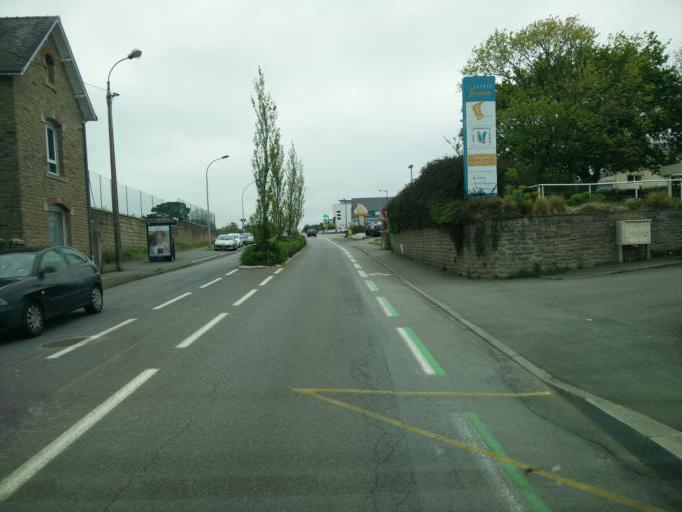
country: FR
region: Brittany
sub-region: Departement du Finistere
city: Concarneau
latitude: 47.8814
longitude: -3.9195
